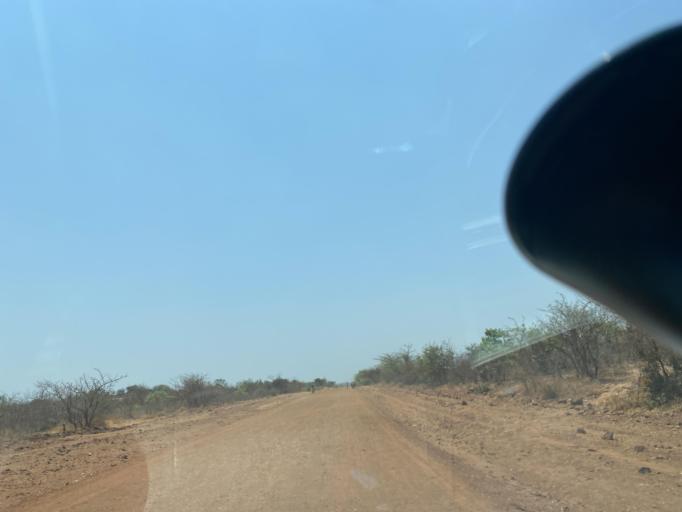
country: ZM
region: Lusaka
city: Lusaka
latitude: -15.4455
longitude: 27.9605
